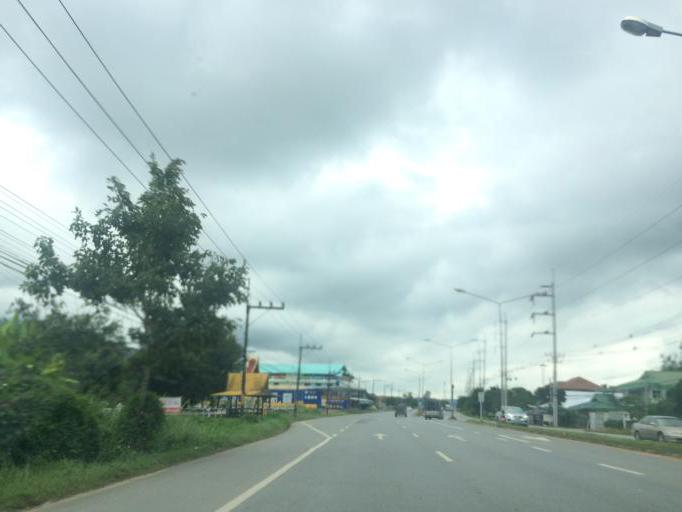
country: TH
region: Chiang Rai
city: Mae Chan
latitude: 20.0841
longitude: 99.8746
